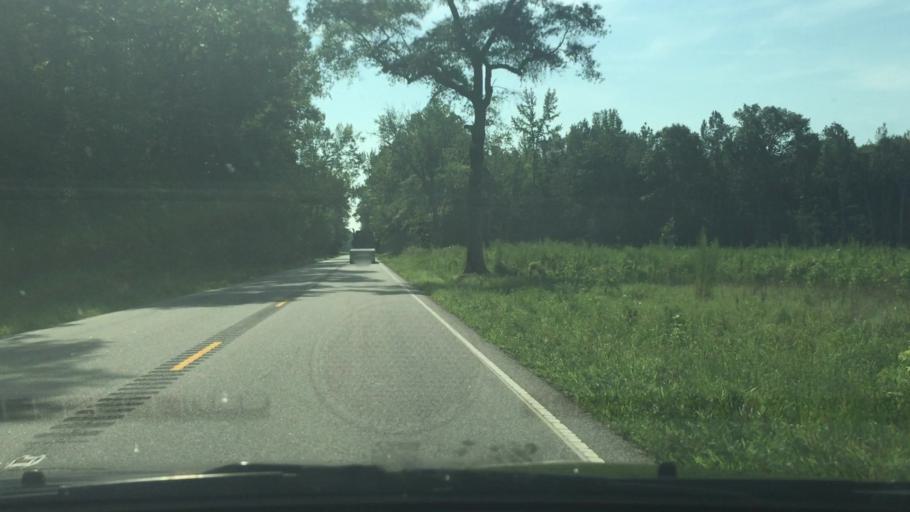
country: US
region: Virginia
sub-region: Sussex County
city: Sussex
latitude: 36.9882
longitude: -77.2512
